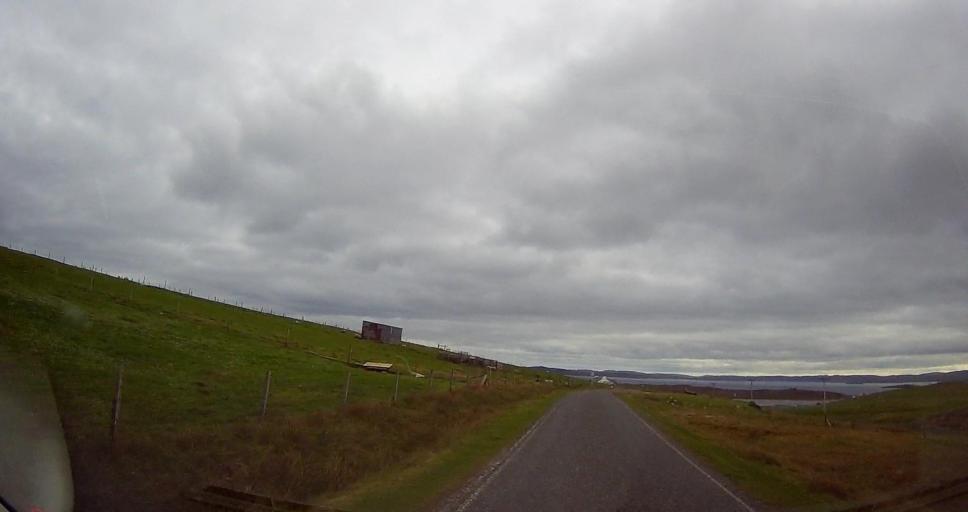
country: GB
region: Scotland
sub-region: Shetland Islands
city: Shetland
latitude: 60.5082
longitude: -1.0585
